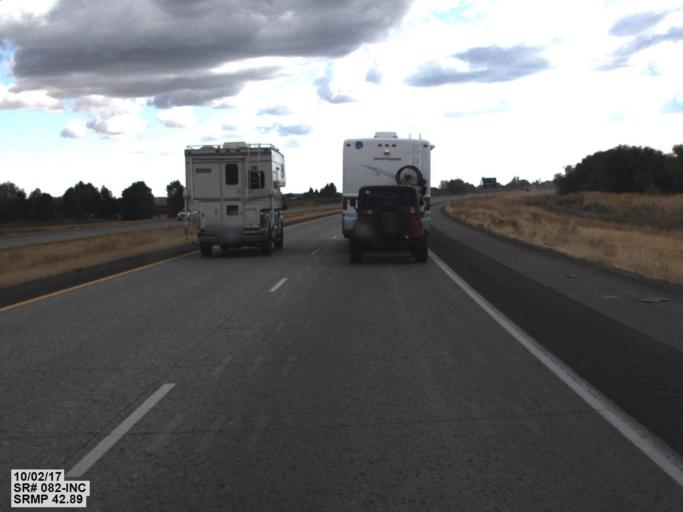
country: US
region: Washington
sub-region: Yakima County
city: Wapato
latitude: 46.4867
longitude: -120.4159
